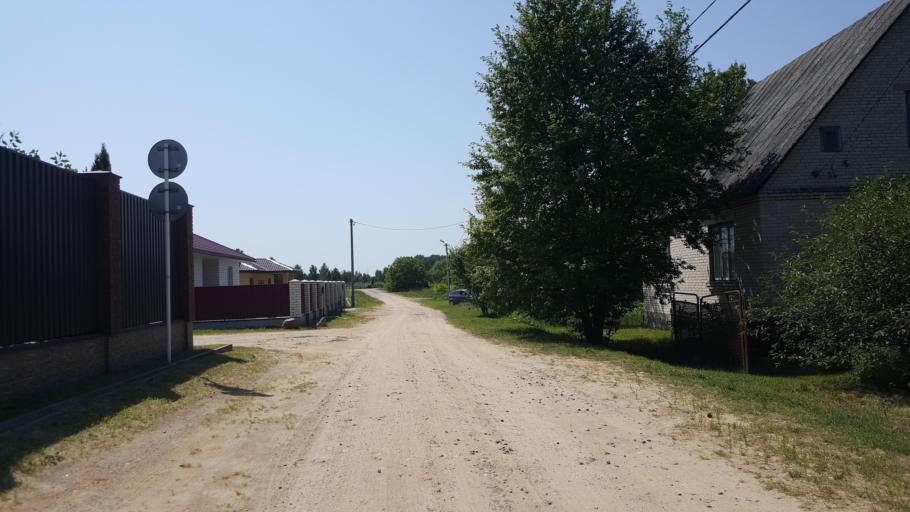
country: BY
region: Brest
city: Zhabinka
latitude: 52.1975
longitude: 23.9903
